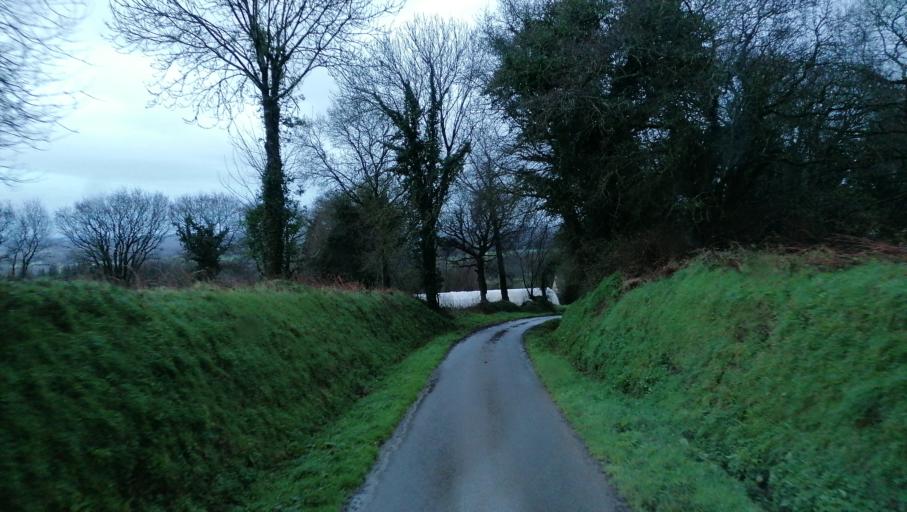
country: FR
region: Brittany
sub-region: Departement des Cotes-d'Armor
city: Plouagat
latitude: 48.4816
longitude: -2.9870
